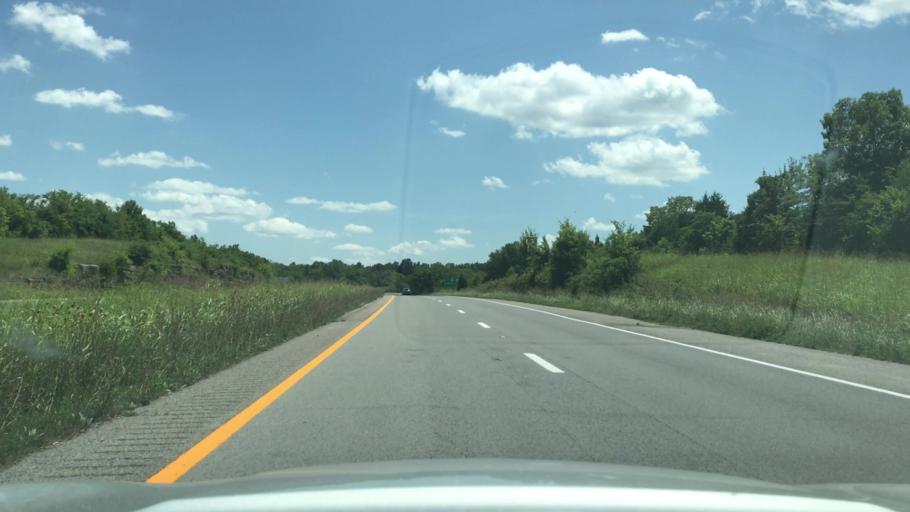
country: US
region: Kentucky
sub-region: Christian County
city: Hopkinsville
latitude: 36.8803
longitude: -87.4687
